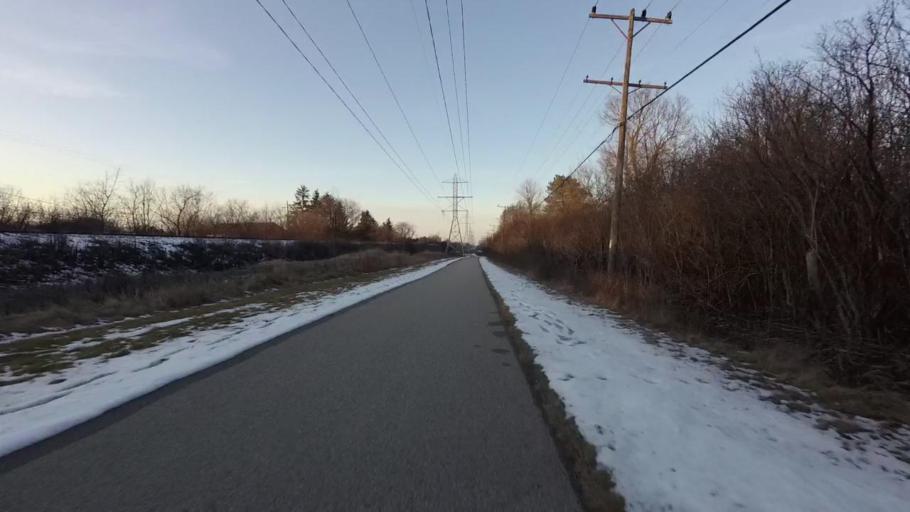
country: US
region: Wisconsin
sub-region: Milwaukee County
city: Brown Deer
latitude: 43.1685
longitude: -87.9631
